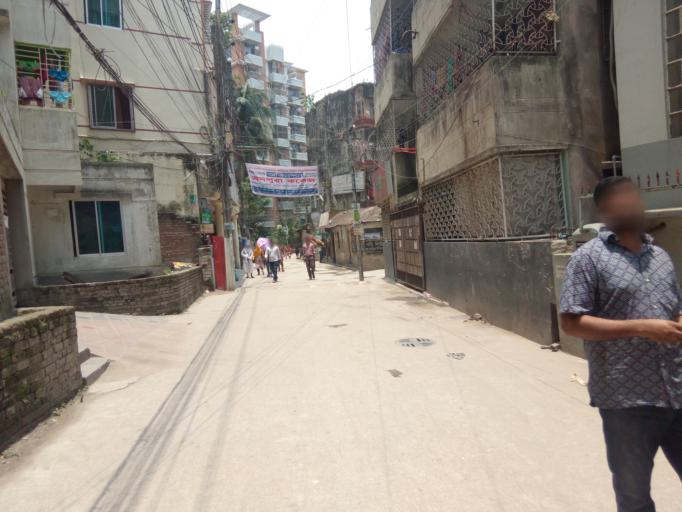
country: BD
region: Dhaka
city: Paltan
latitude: 23.7563
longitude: 90.4156
